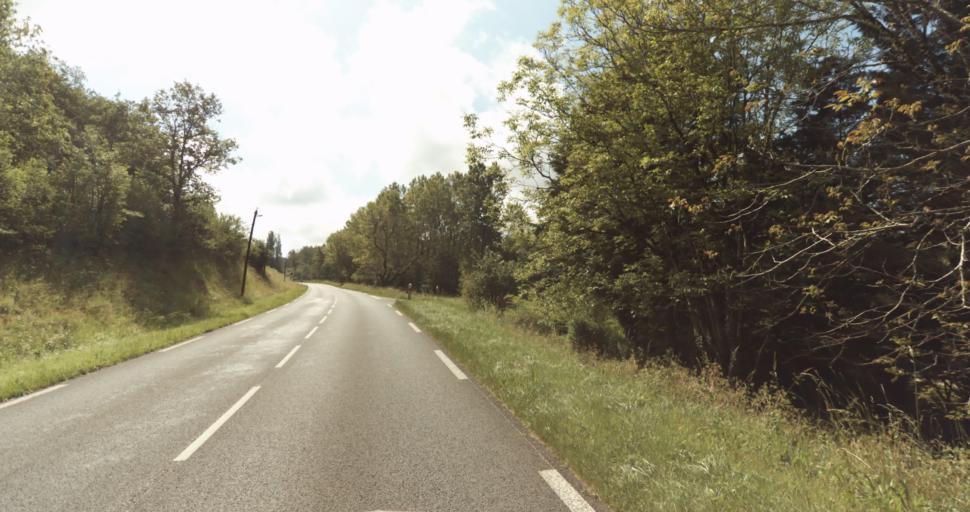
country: FR
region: Aquitaine
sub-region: Departement de la Dordogne
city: Le Bugue
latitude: 44.8417
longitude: 0.8524
